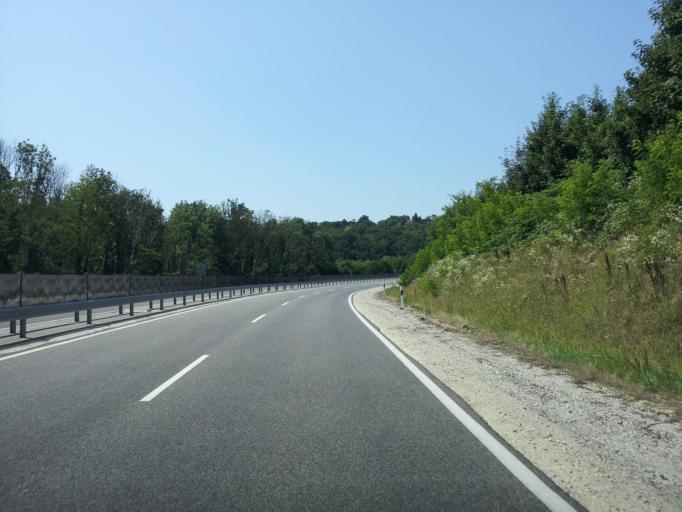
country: HU
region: Zala
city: Zalaegerszeg
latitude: 46.8357
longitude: 16.8911
